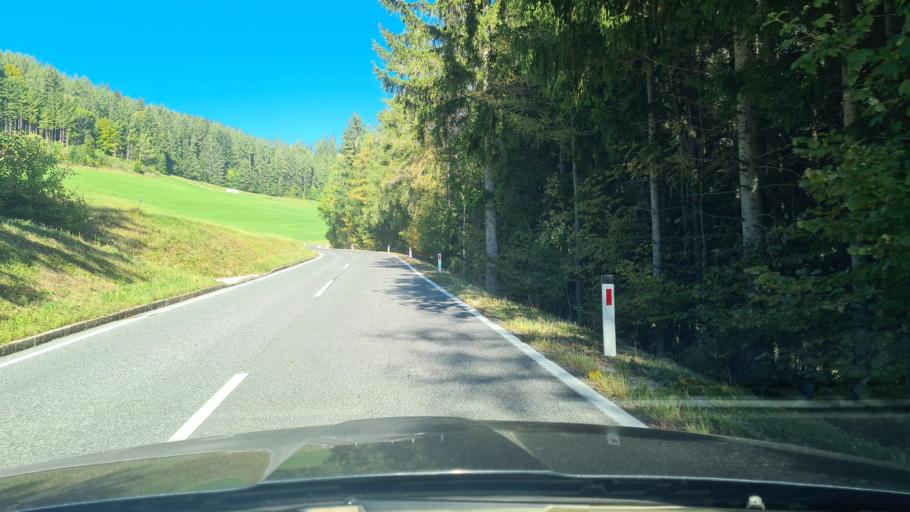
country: AT
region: Styria
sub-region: Politischer Bezirk Weiz
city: Passail
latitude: 47.3042
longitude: 15.4863
